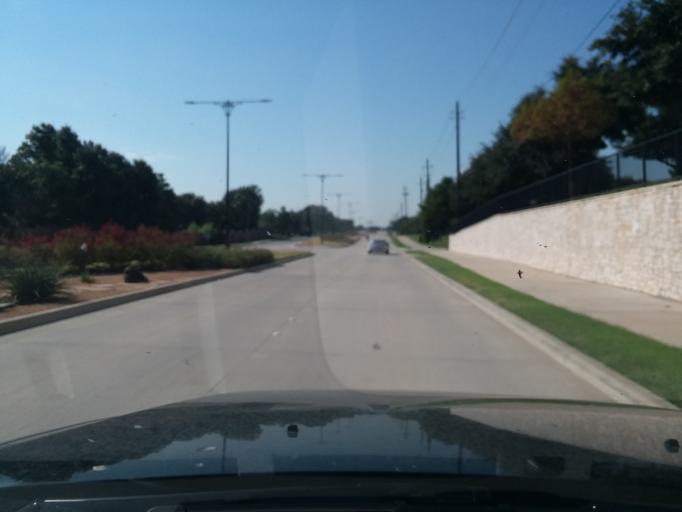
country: US
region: Texas
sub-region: Dallas County
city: Coppell
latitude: 32.9706
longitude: -97.0152
